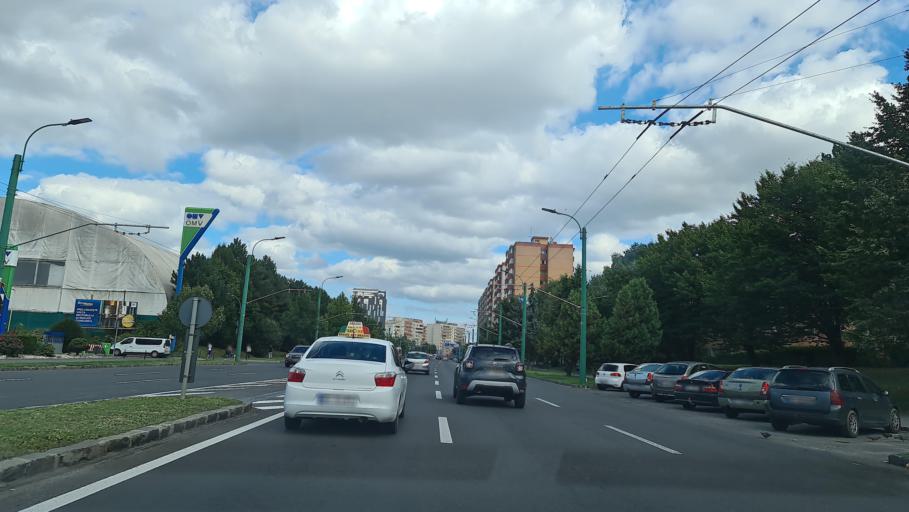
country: RO
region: Brasov
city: Brasov
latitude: 45.6598
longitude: 25.6148
